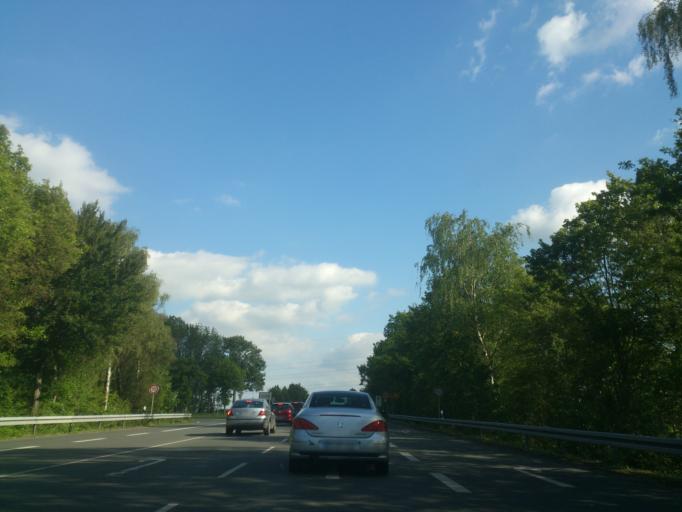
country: DE
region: North Rhine-Westphalia
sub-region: Regierungsbezirk Detmold
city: Paderborn
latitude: 51.7042
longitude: 8.7792
